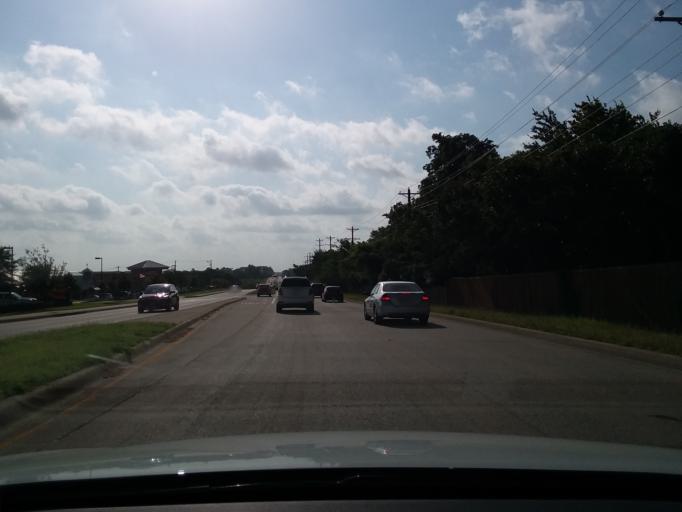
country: US
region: Texas
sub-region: Denton County
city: Double Oak
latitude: 33.0722
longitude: -97.1118
